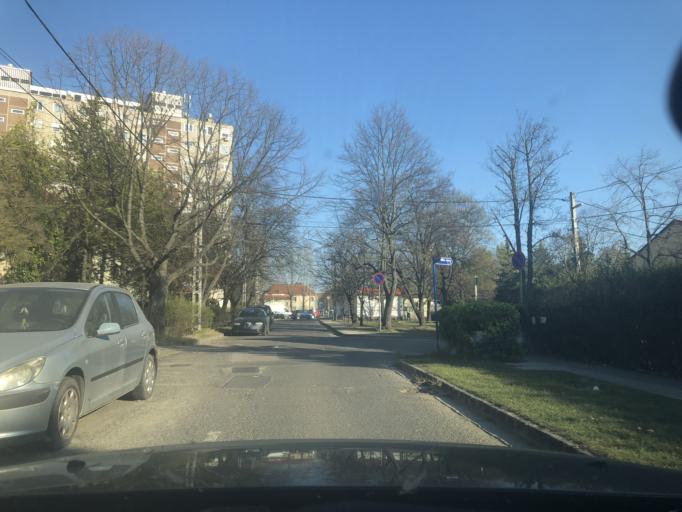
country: HU
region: Pest
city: Dunakeszi
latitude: 47.6456
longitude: 19.1285
